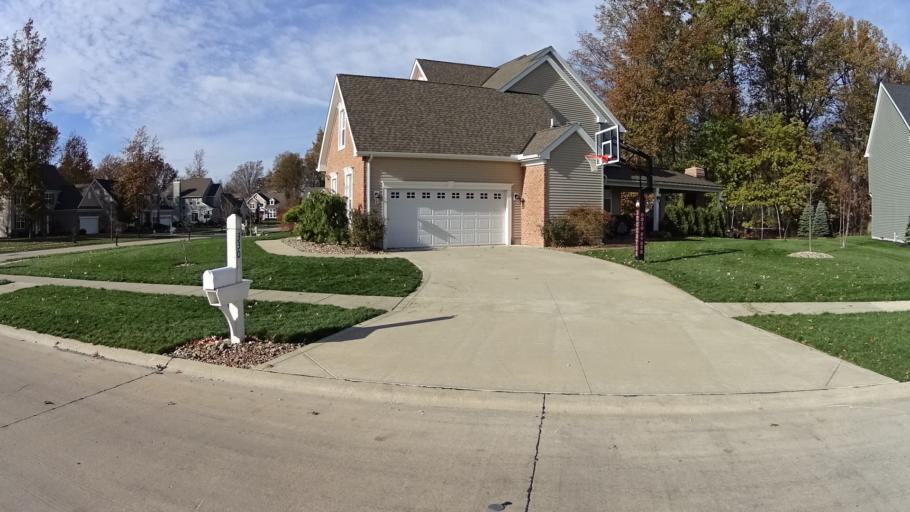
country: US
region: Ohio
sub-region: Lorain County
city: Avon Lake
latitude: 41.4960
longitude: -82.0409
